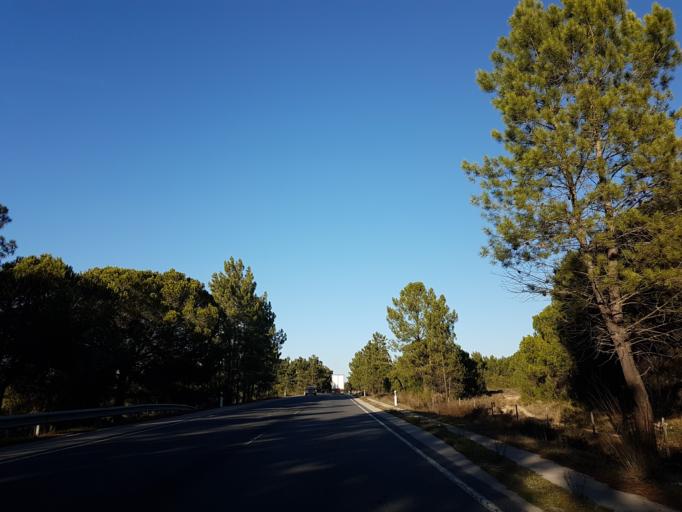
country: PT
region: Setubal
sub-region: Alcacer do Sal
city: Alcacer do Sal
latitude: 38.3884
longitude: -8.5230
